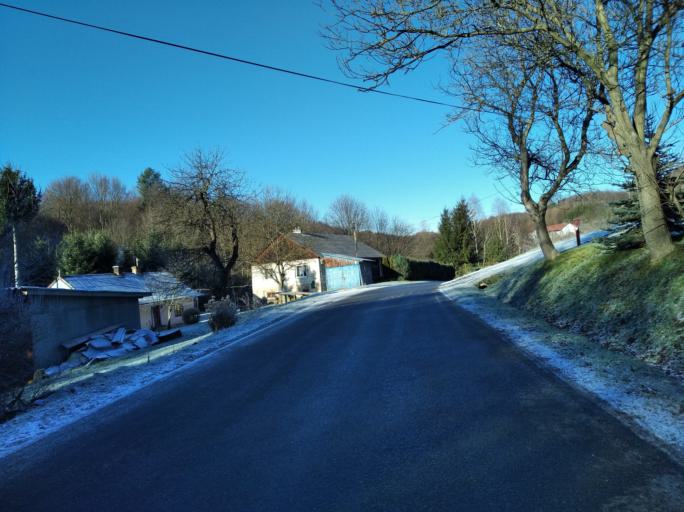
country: PL
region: Subcarpathian Voivodeship
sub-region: Powiat ropczycko-sedziszowski
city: Iwierzyce
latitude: 49.9560
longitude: 21.7649
